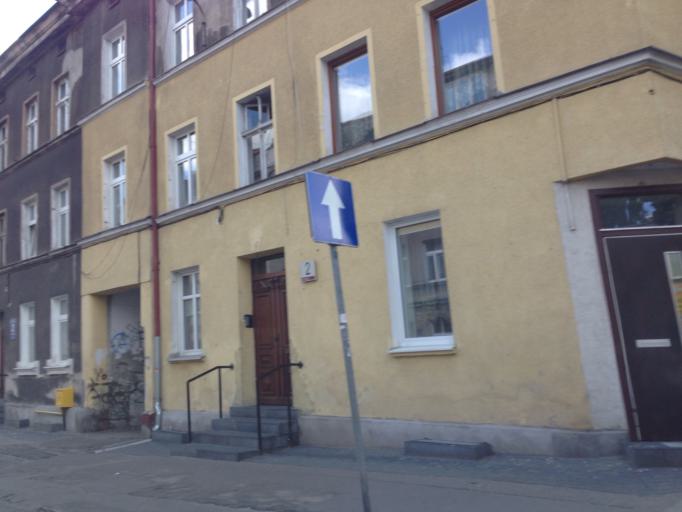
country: PL
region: Pomeranian Voivodeship
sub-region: Gdansk
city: Gdansk
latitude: 54.3834
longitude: 18.6129
